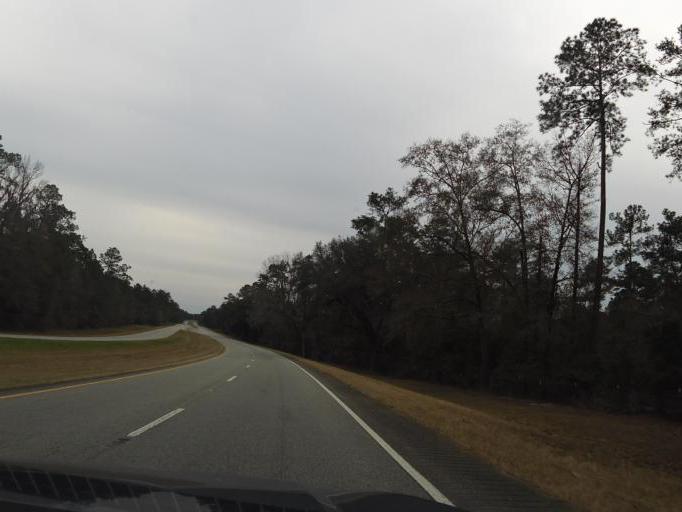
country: US
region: Florida
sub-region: Jefferson County
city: Monticello
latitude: 30.6758
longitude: -83.8868
